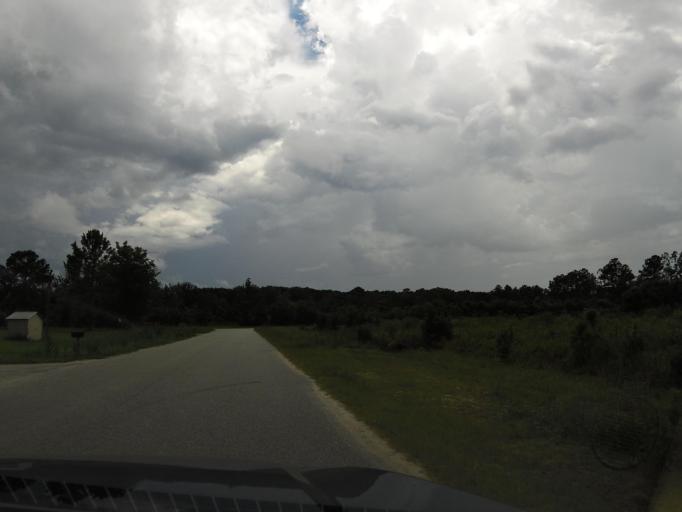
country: US
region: Georgia
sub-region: Camden County
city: Kingsland
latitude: 30.7821
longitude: -81.6376
